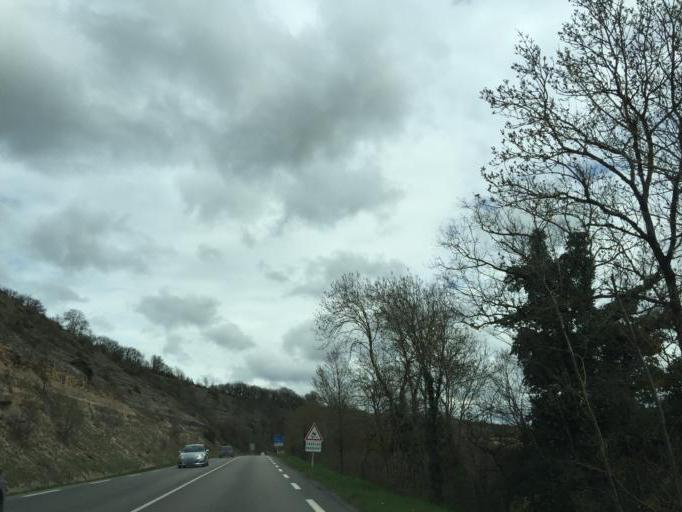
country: FR
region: Midi-Pyrenees
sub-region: Departement de l'Aveyron
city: La Loubiere
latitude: 44.3736
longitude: 2.6366
